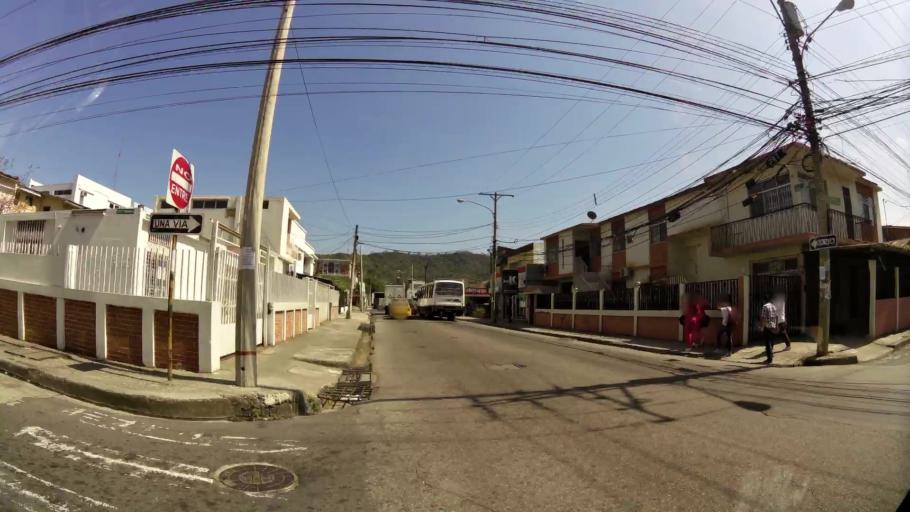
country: EC
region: Guayas
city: Guayaquil
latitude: -2.1628
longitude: -79.9130
